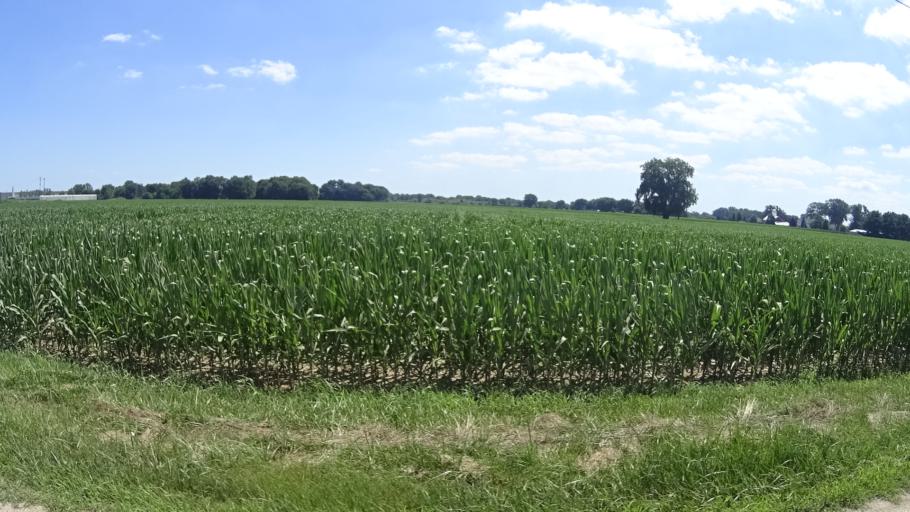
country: US
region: Ohio
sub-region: Erie County
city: Huron
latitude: 41.3914
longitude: -82.5908
